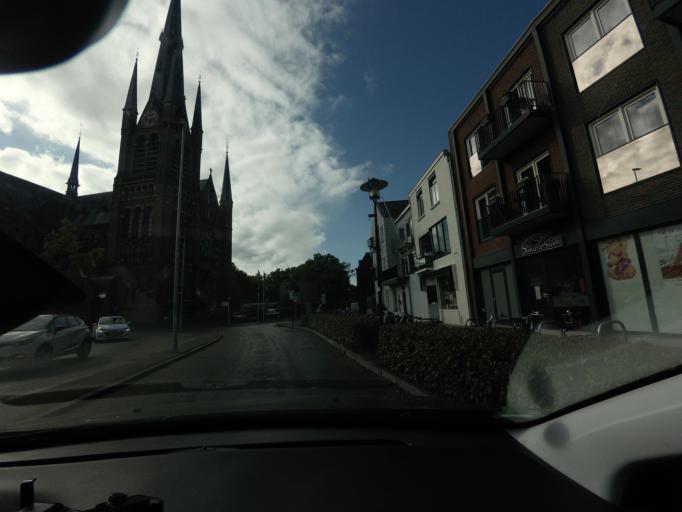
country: NL
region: Utrecht
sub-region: Gemeente Woerden
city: Woerden
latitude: 52.1006
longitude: 4.9213
